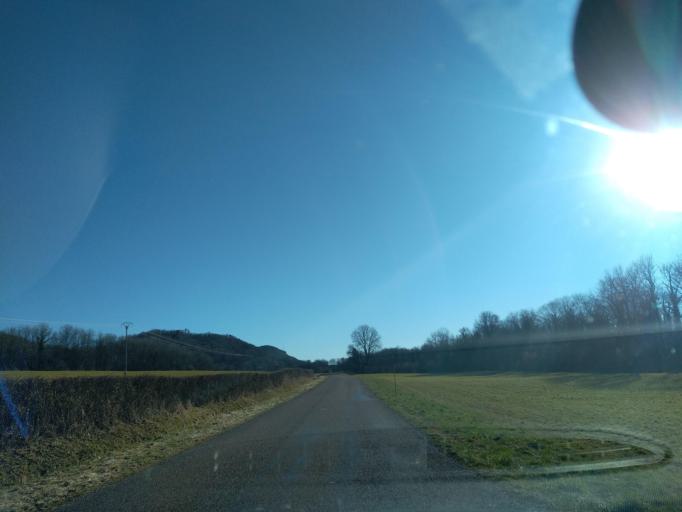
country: FR
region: Franche-Comte
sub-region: Departement du Jura
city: Poligny
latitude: 46.7119
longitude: 5.7370
